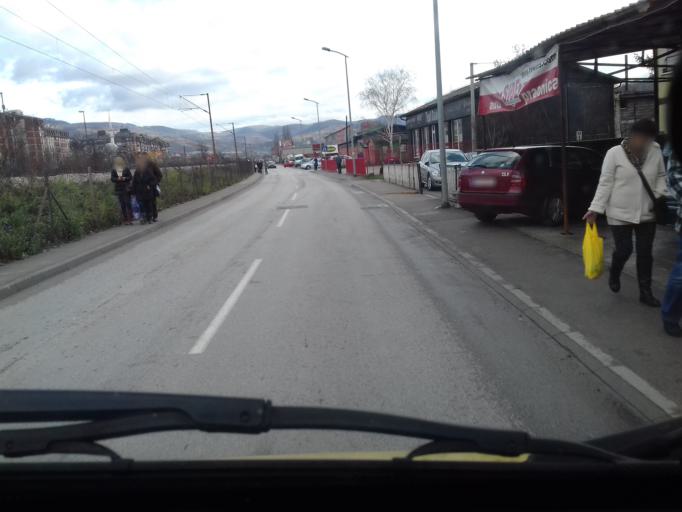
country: BA
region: Federation of Bosnia and Herzegovina
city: Zenica
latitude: 44.1945
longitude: 17.9260
